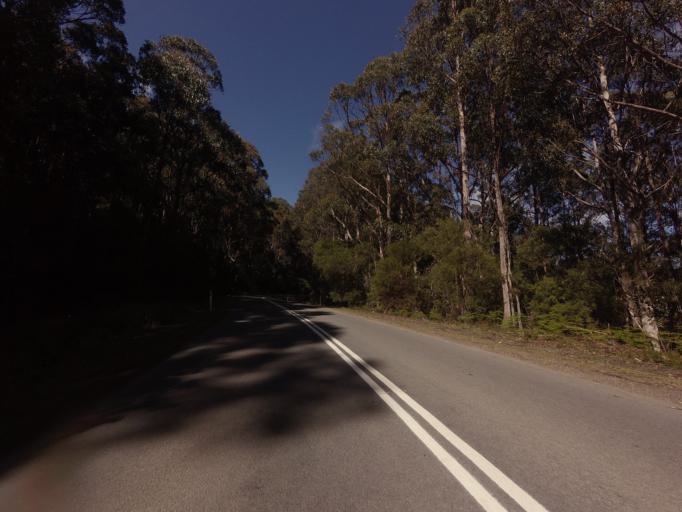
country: AU
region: Tasmania
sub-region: Derwent Valley
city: New Norfolk
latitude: -42.7293
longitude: 146.6703
